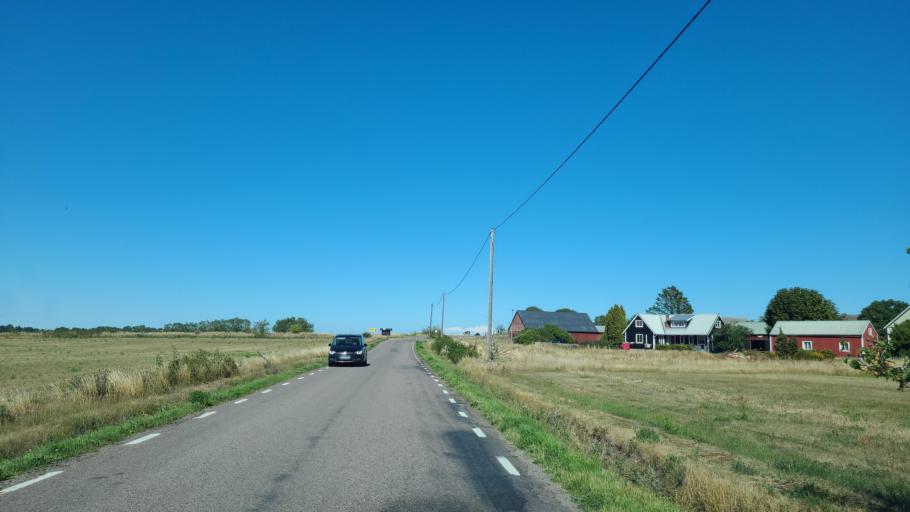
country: SE
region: Kalmar
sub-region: Borgholms Kommun
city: Borgholm
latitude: 56.8584
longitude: 16.8144
